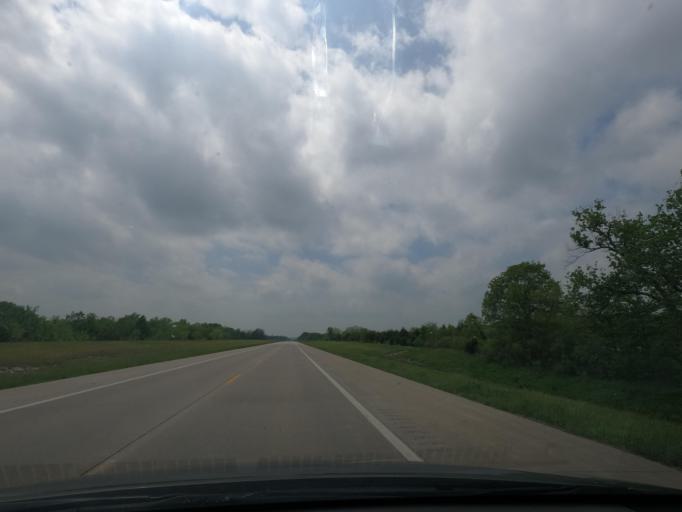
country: US
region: Kansas
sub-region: Labette County
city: Parsons
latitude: 37.3486
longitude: -95.3289
